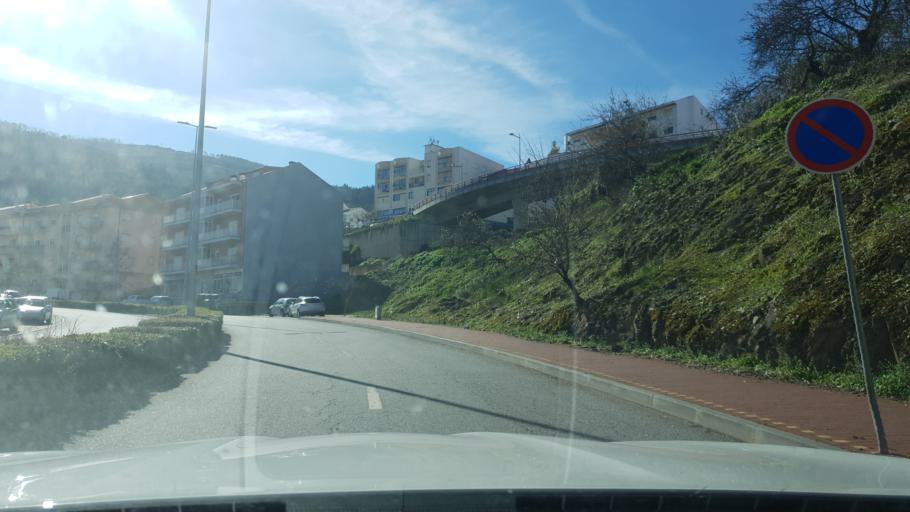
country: PT
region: Braganca
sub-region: Torre de Moncorvo
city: Torre de Moncorvo
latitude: 41.1757
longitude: -7.0504
